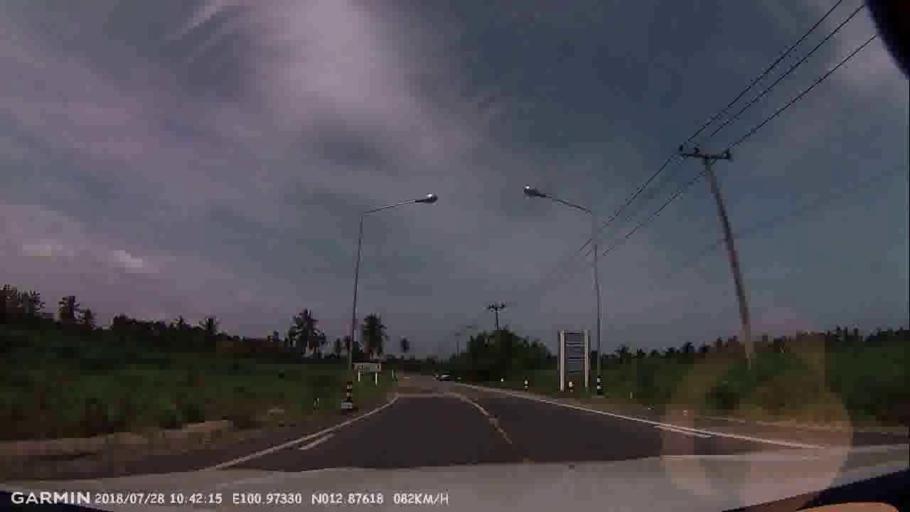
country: TH
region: Chon Buri
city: Phatthaya
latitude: 12.8762
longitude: 100.9731
